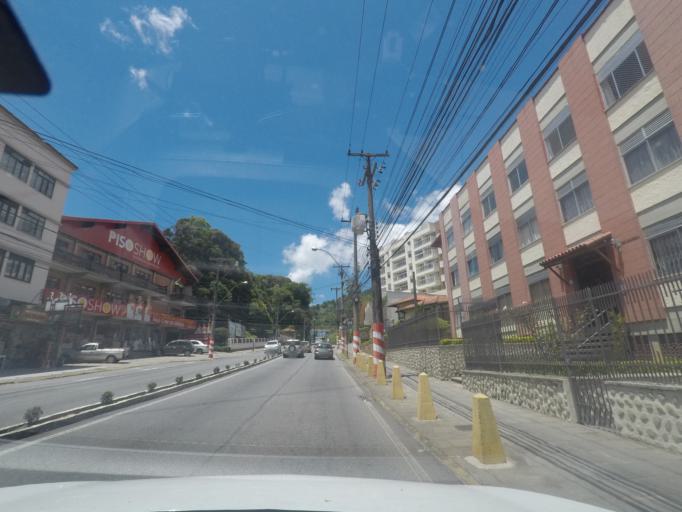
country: BR
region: Rio de Janeiro
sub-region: Teresopolis
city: Teresopolis
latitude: -22.4262
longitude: -42.9799
